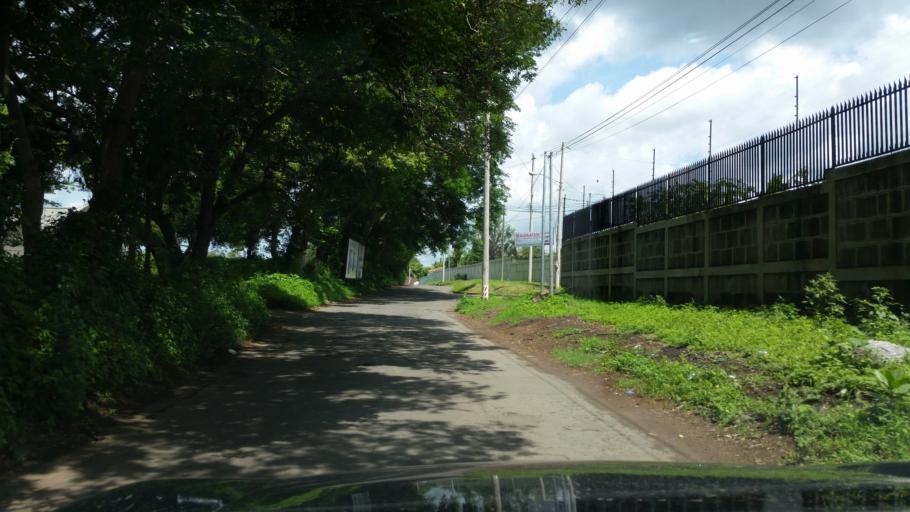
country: NI
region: Managua
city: Managua
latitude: 12.0890
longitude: -86.2216
